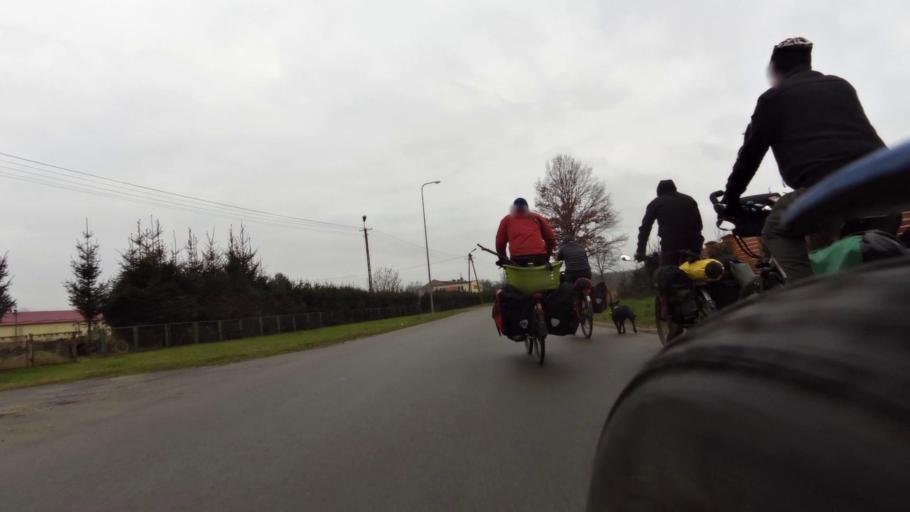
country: PL
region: West Pomeranian Voivodeship
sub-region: Powiat szczecinecki
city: Szczecinek
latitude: 53.6840
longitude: 16.6765
